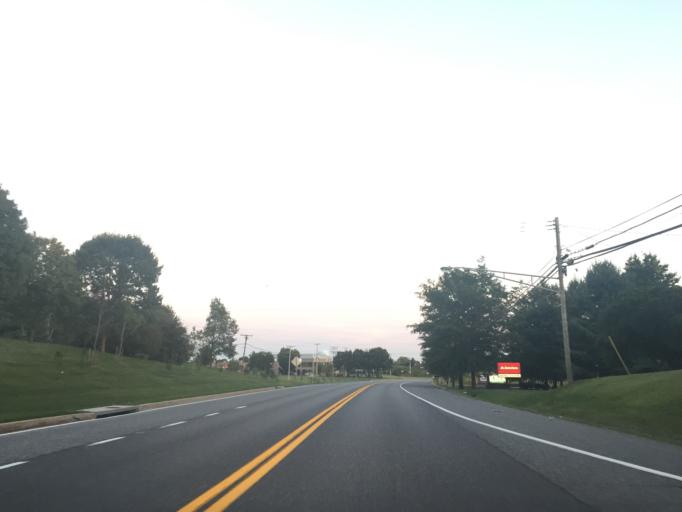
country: US
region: Maryland
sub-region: Harford County
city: Bel Air North
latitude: 39.5804
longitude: -76.3870
